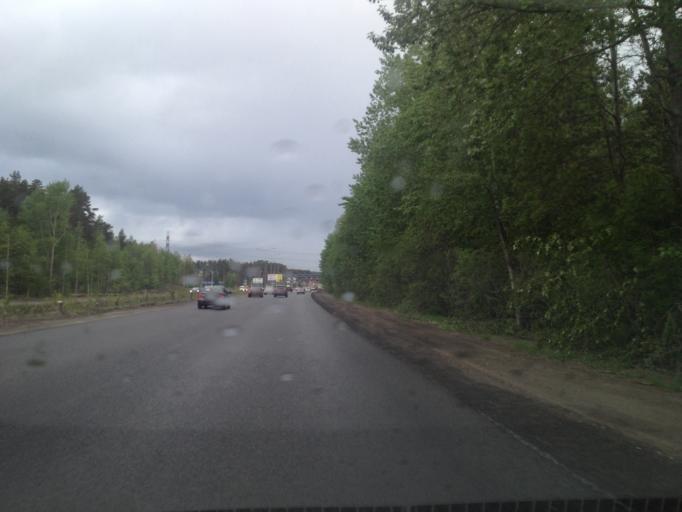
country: RU
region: Sverdlovsk
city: Shirokaya Rechka
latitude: 56.8106
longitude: 60.5231
